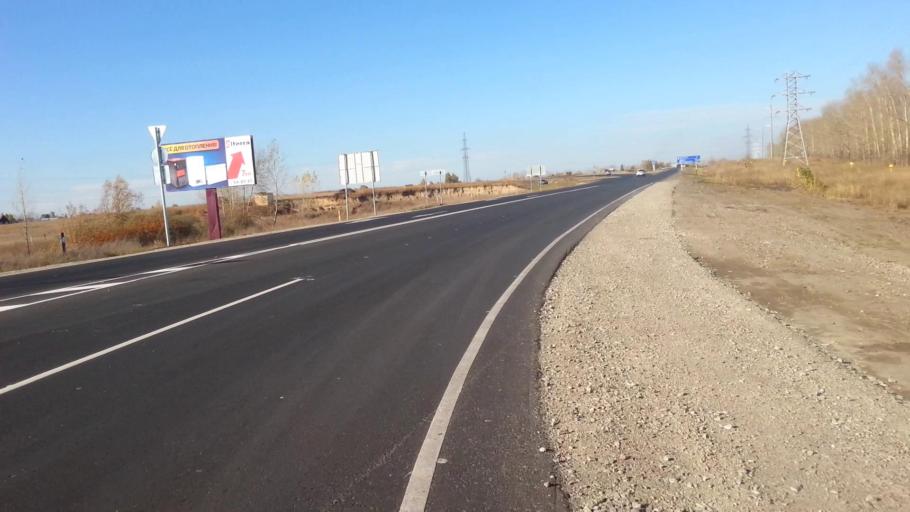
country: RU
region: Altai Krai
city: Sannikovo
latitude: 53.3370
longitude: 83.9387
